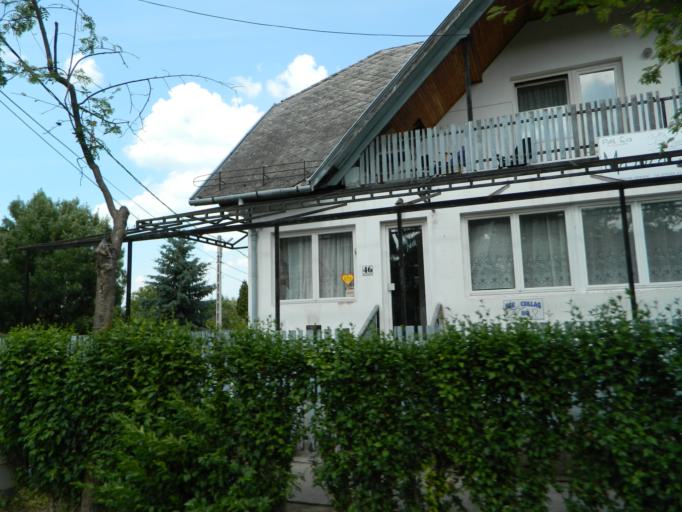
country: HU
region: Somogy
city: Balatonfoldvar
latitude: 46.8448
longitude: 17.8824
